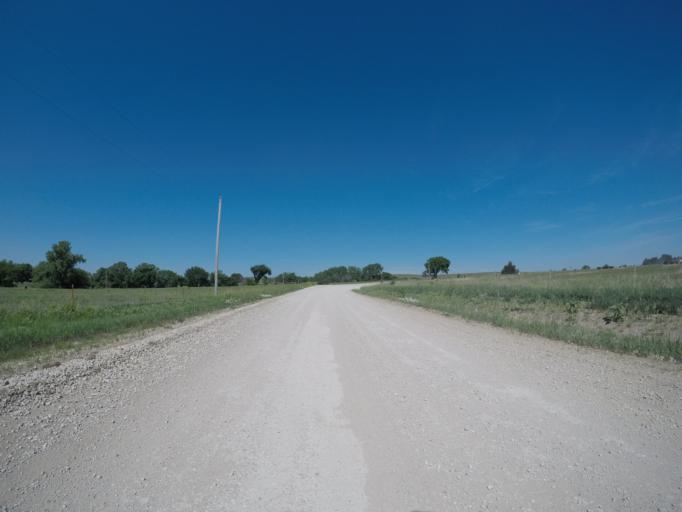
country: US
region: Kansas
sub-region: Wabaunsee County
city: Alma
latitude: 39.0224
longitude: -96.1489
